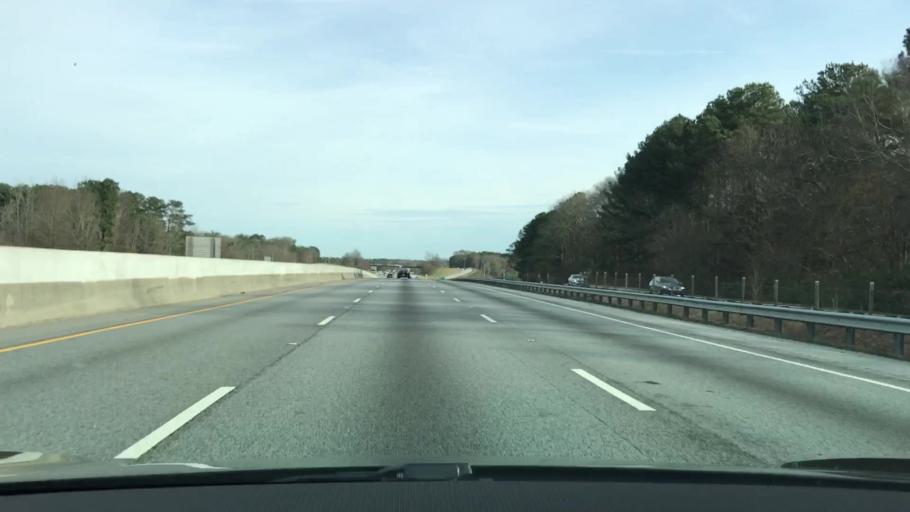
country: US
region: Georgia
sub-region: Rockdale County
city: Conyers
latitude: 33.6295
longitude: -83.9565
